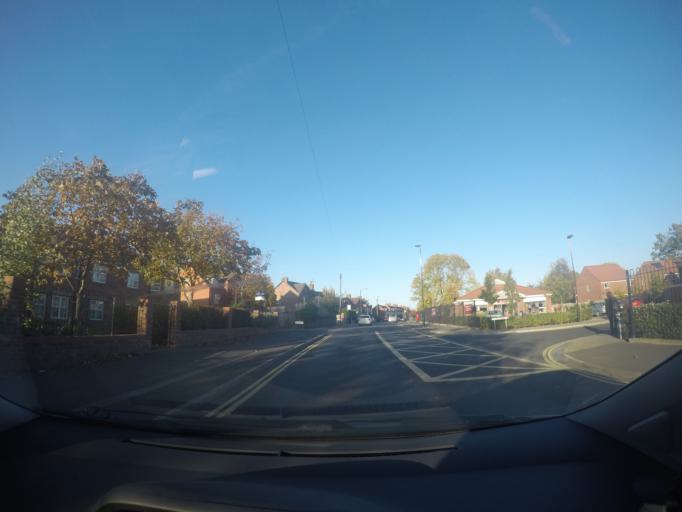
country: GB
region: England
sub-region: City of York
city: York
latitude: 53.9758
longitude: -1.0731
